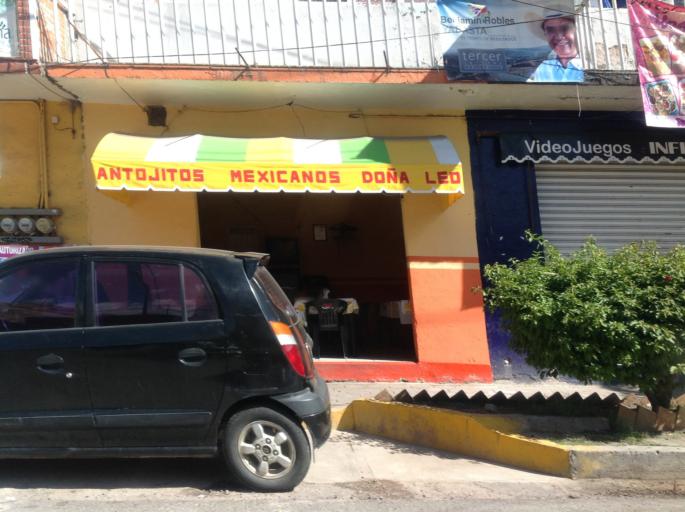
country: MX
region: Oaxaca
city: Ciudad de Huajuapam de Leon
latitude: 17.8114
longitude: -97.7736
